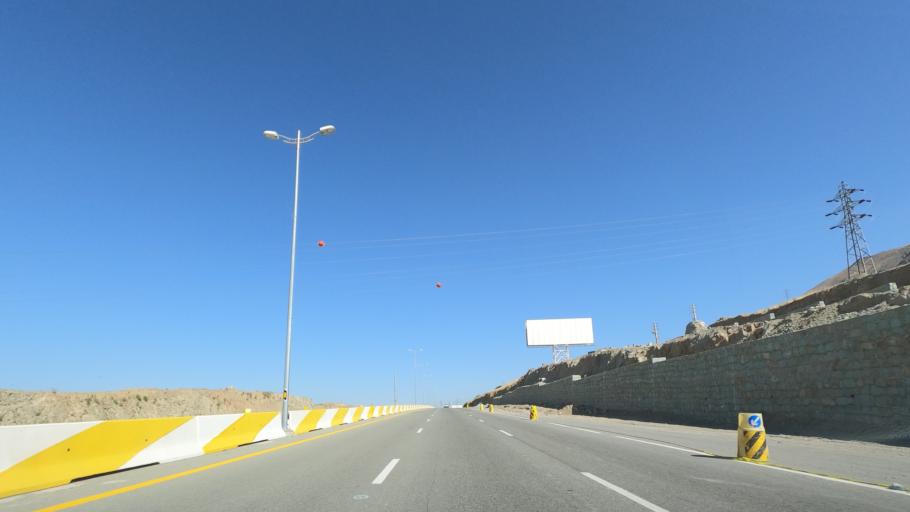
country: IR
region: Tehran
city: Shahr-e Qods
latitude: 35.7656
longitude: 51.0681
